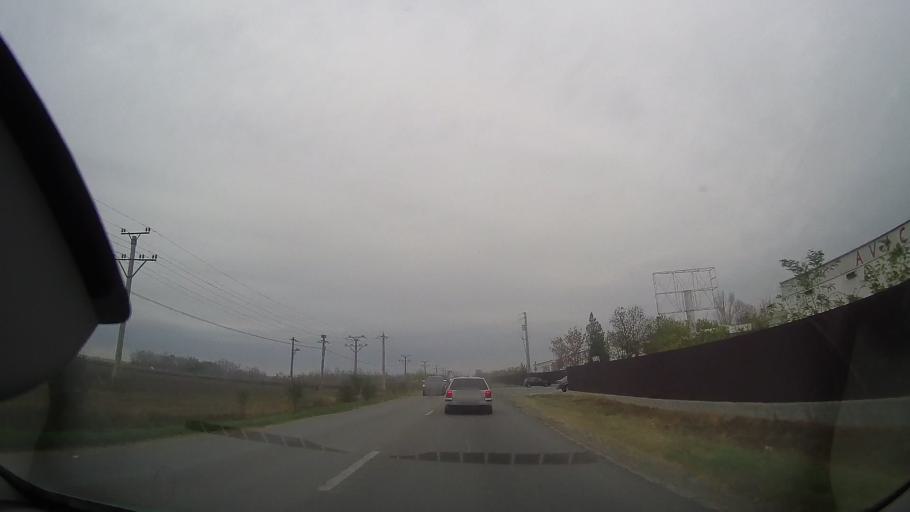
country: RO
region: Ialomita
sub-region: Oras Amara
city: Amara
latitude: 44.5885
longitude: 27.3314
